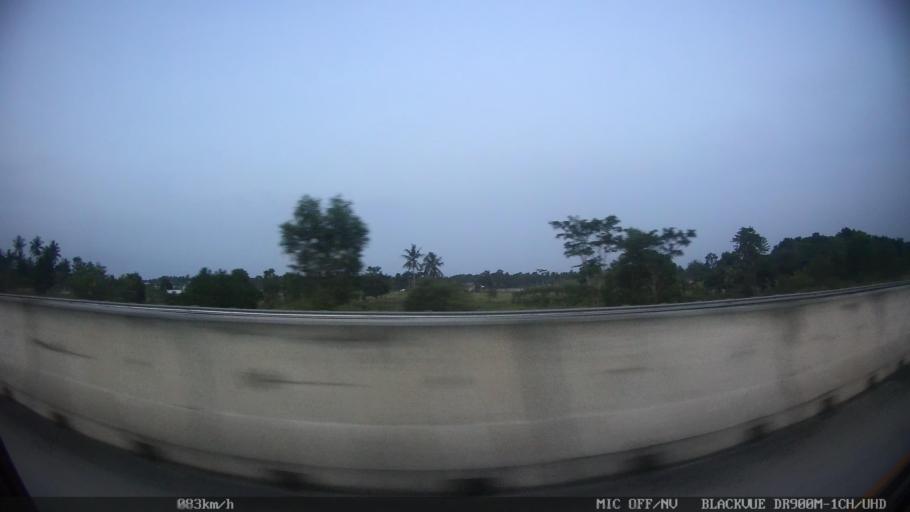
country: ID
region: Lampung
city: Sidorejo
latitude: -5.6378
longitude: 105.5703
